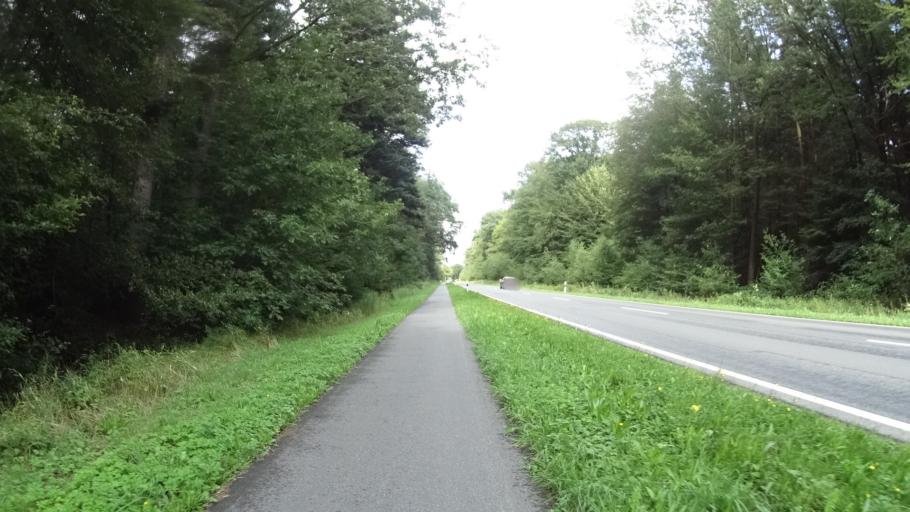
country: DE
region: Lower Saxony
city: Varel
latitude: 53.3870
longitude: 8.0766
